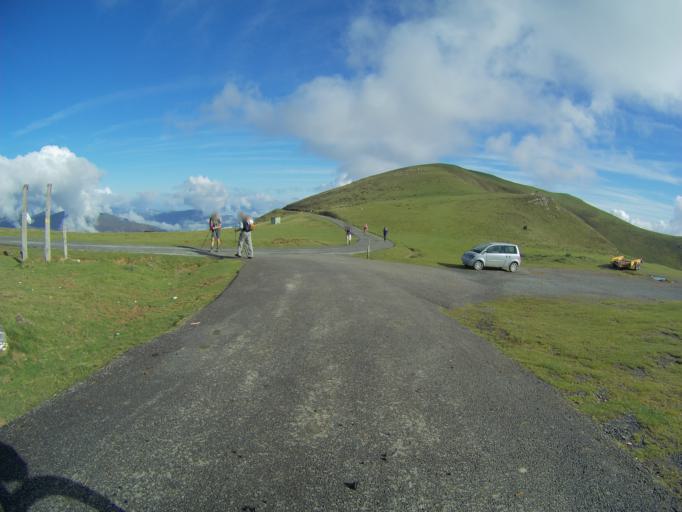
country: FR
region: Aquitaine
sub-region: Departement des Pyrenees-Atlantiques
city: Saint-Jean-Pied-de-Port
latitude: 43.0810
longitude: -1.2523
